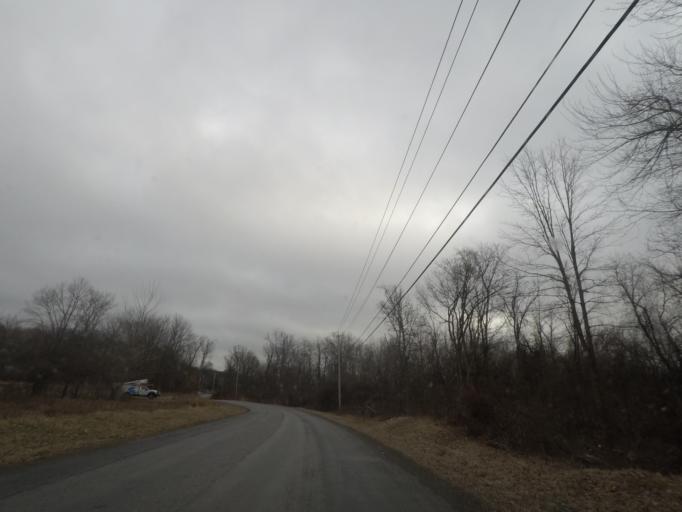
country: US
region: New York
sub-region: Saratoga County
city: Waterford
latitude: 42.7689
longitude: -73.6560
